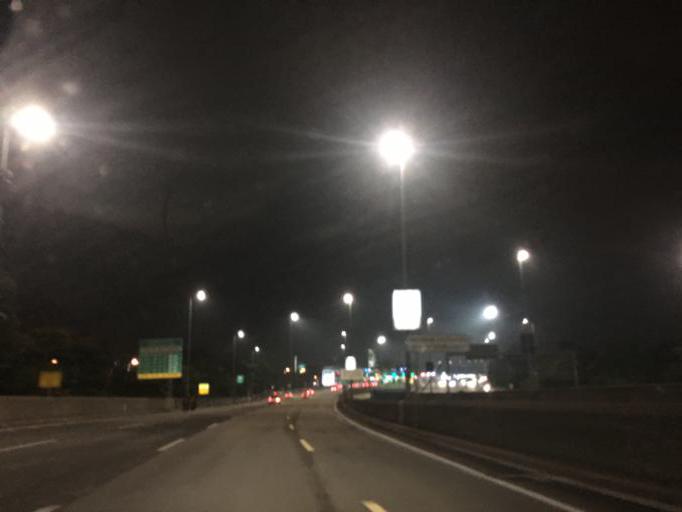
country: MY
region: Kuala Lumpur
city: Kuala Lumpur
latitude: 3.1662
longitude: 101.7183
